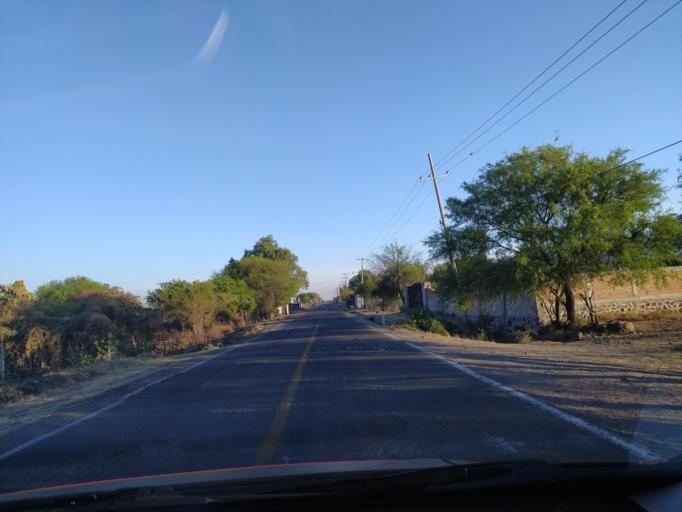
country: MX
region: Guanajuato
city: Ciudad Manuel Doblado
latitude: 20.7466
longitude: -101.8238
